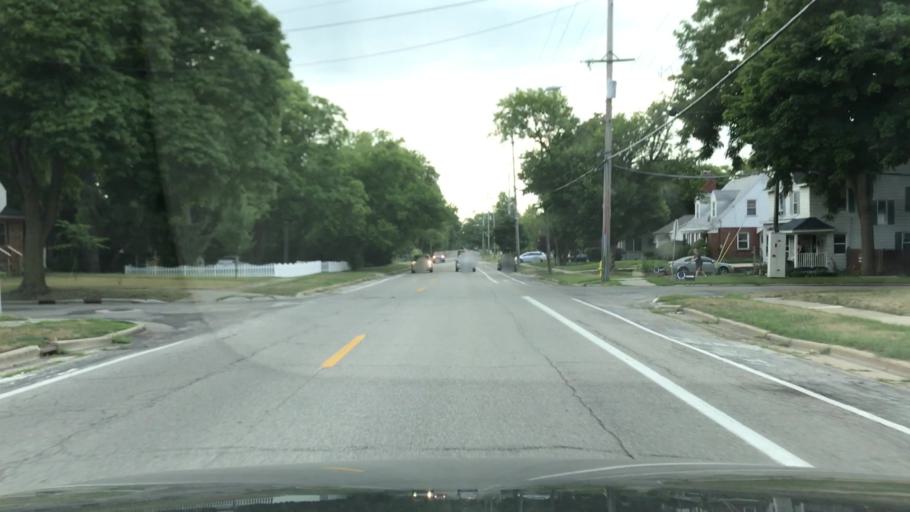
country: US
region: Michigan
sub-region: Kent County
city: Grand Rapids
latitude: 42.9989
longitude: -85.6471
